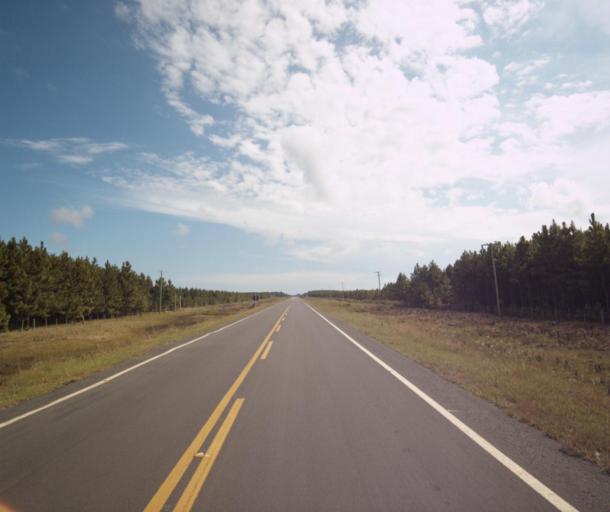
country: BR
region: Rio Grande do Sul
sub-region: Sao Lourenco Do Sul
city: Sao Lourenco do Sul
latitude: -31.5932
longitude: -51.3714
